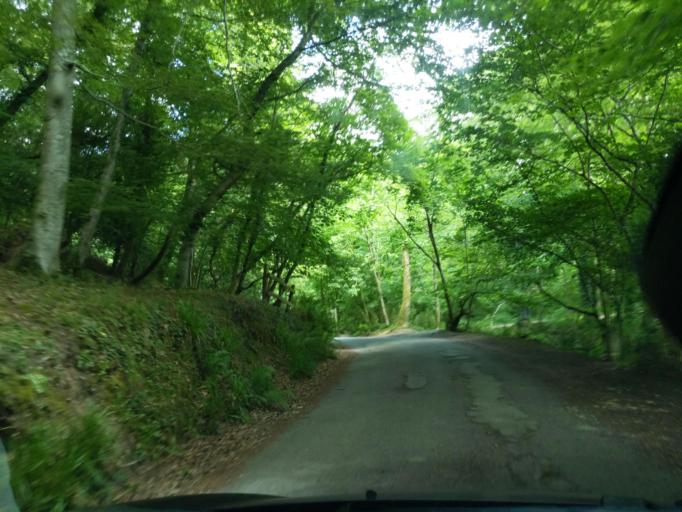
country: GB
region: England
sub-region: Devon
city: Plympton
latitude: 50.4090
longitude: -4.0834
